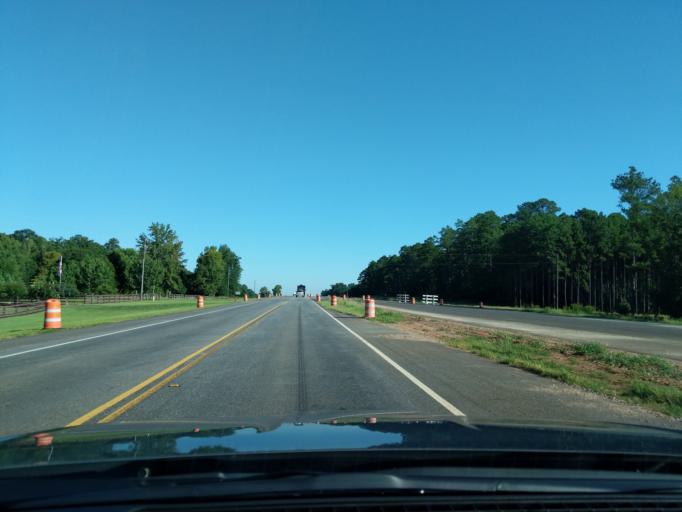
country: US
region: Georgia
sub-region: McDuffie County
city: Thomson
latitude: 33.5592
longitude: -82.5145
